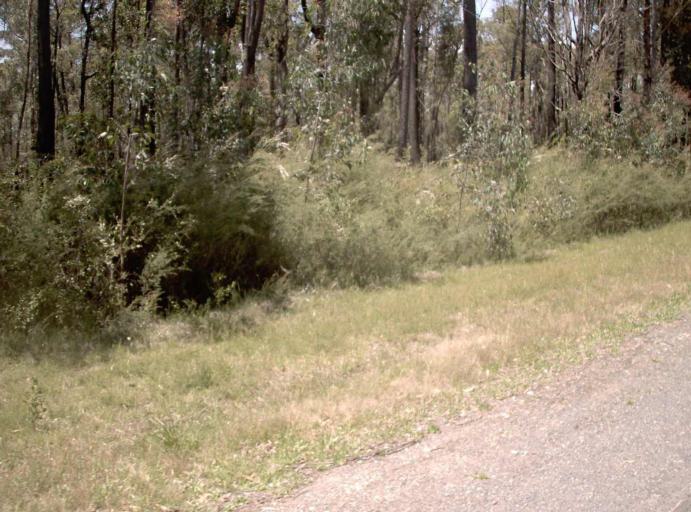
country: AU
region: Victoria
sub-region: East Gippsland
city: Lakes Entrance
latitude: -37.6927
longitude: 148.6294
